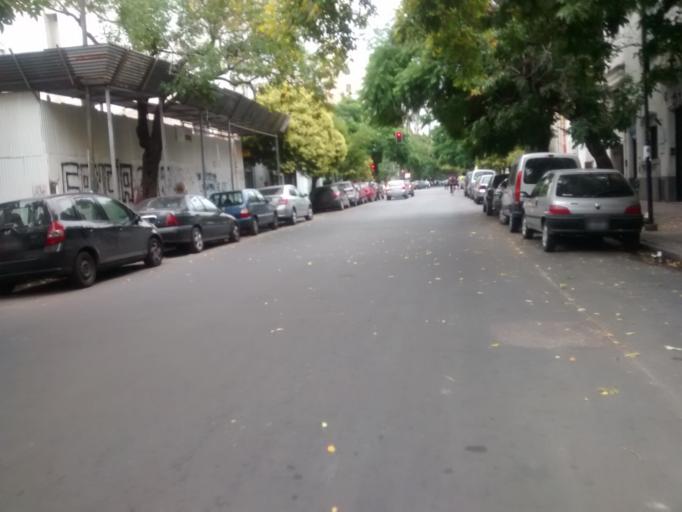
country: AR
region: Buenos Aires
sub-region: Partido de La Plata
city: La Plata
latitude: -34.9149
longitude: -57.9439
